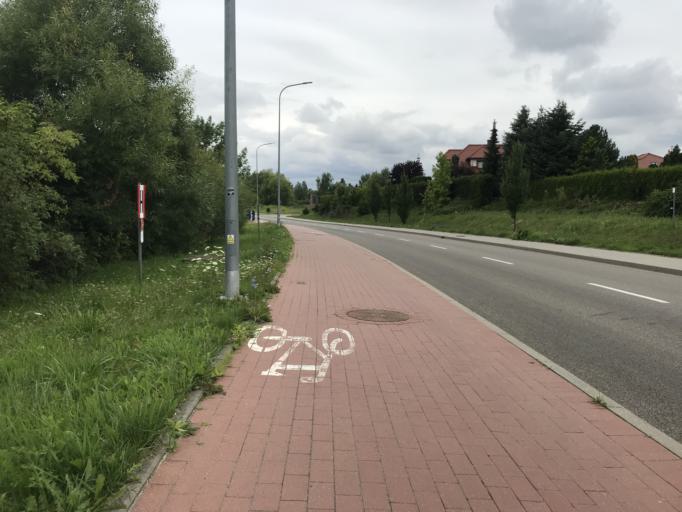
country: PL
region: Warmian-Masurian Voivodeship
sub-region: Powiat elblaski
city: Elblag
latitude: 54.1698
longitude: 19.4349
